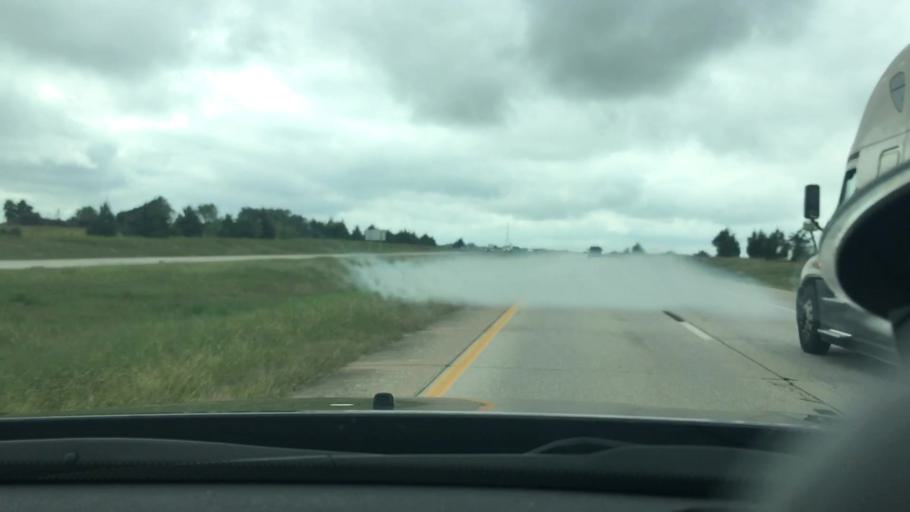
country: US
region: Oklahoma
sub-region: Bryan County
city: Durant
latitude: 34.1606
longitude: -96.2581
